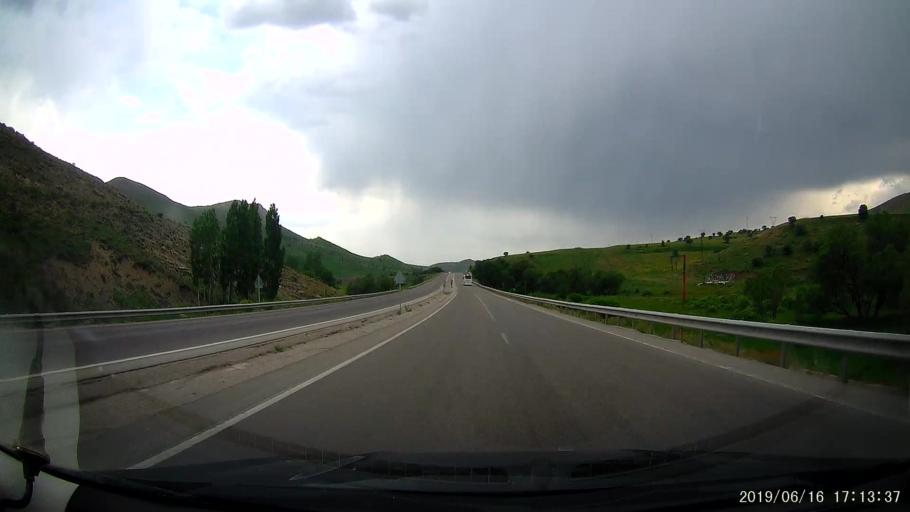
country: TR
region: Erzurum
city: Askale
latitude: 39.8581
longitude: 40.5939
